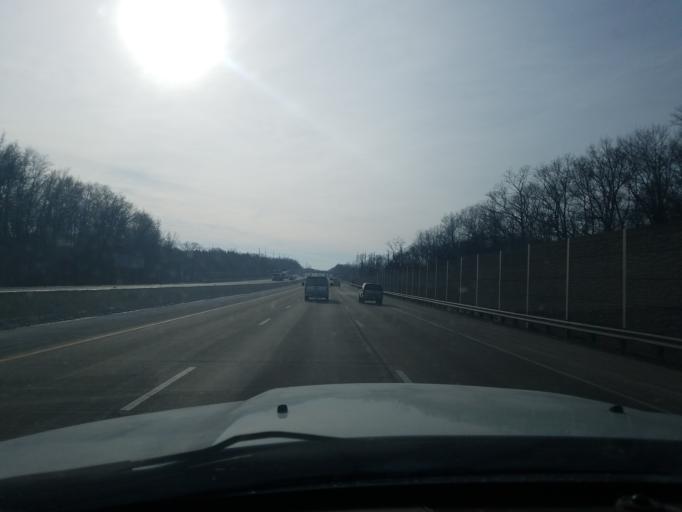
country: US
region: Indiana
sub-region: Allen County
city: Fort Wayne
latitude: 41.0641
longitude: -85.2346
